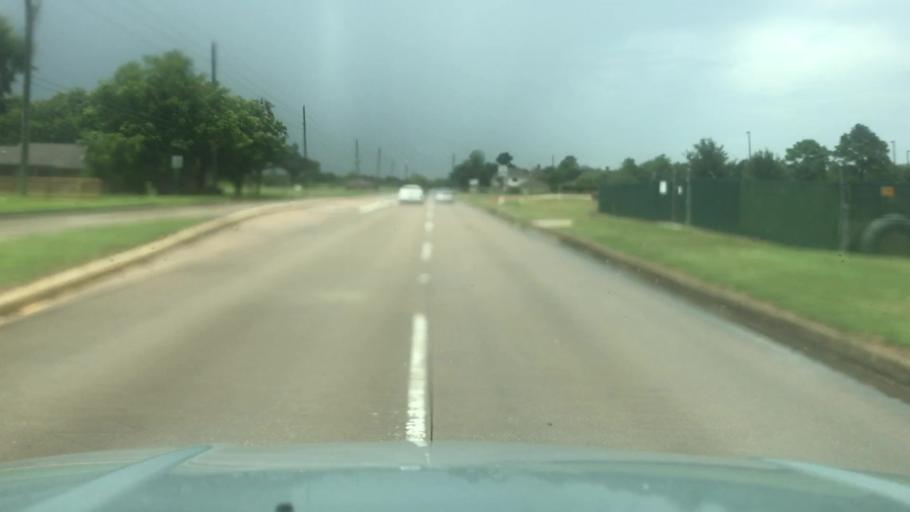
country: US
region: Texas
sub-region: Harris County
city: Katy
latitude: 29.7585
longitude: -95.8081
